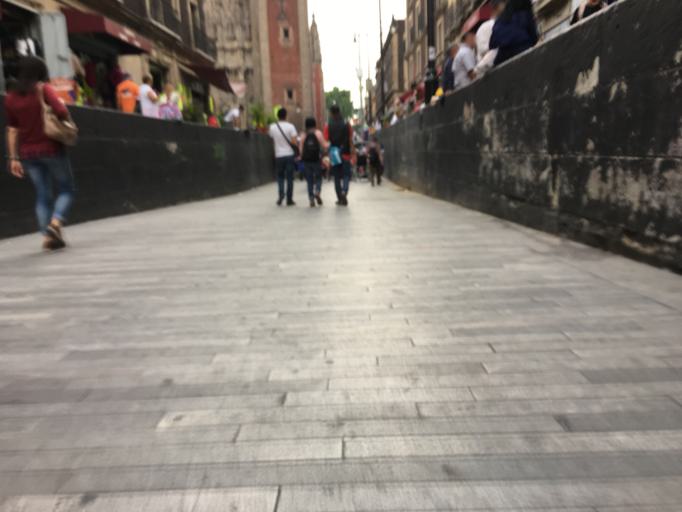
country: MX
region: Mexico City
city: Mexico City
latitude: 19.4331
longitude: -99.1275
